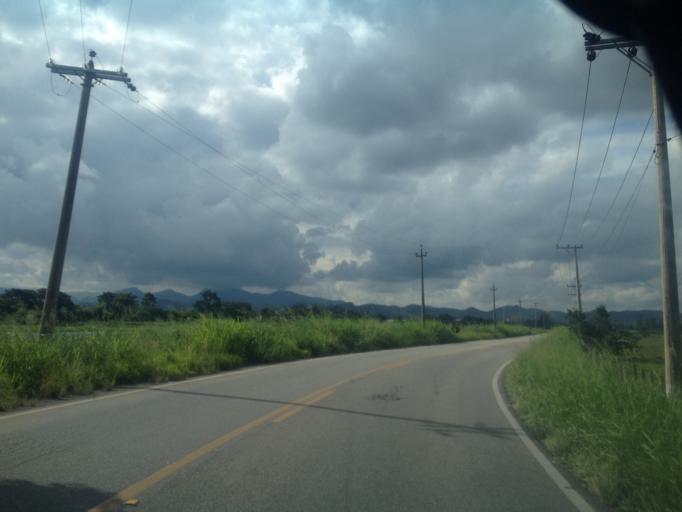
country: BR
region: Rio de Janeiro
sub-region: Porto Real
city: Porto Real
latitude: -22.4356
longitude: -44.2928
